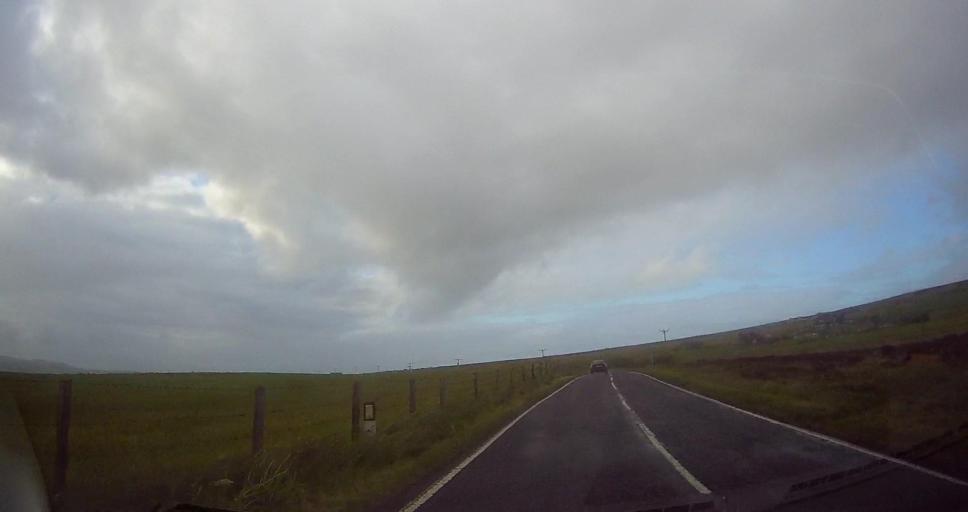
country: GB
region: Scotland
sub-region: Orkney Islands
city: Stromness
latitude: 58.9381
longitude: -3.2135
